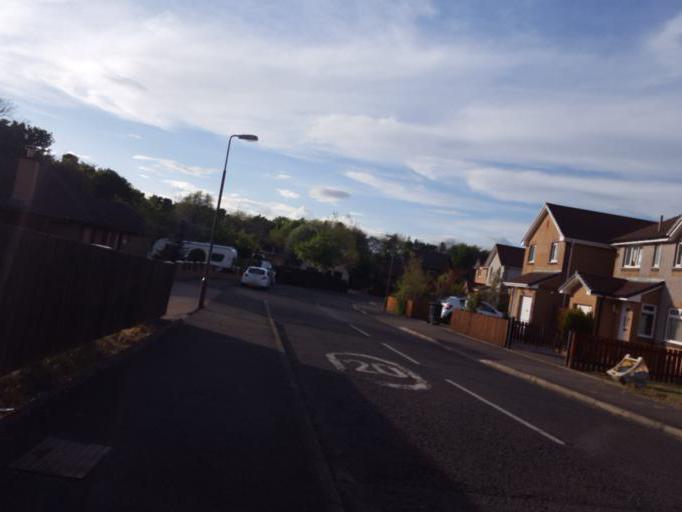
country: GB
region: Scotland
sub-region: West Lothian
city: Livingston
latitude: 55.8998
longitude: -3.5322
